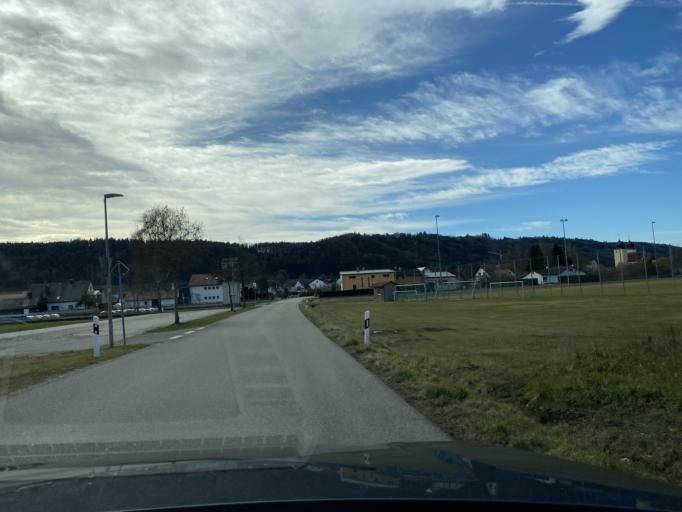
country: DE
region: Bavaria
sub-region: Upper Palatinate
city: Dietfurt
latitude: 49.0210
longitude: 11.5248
